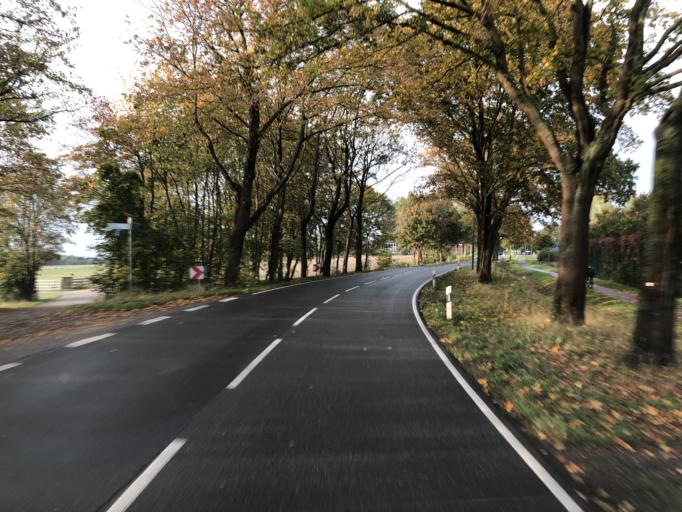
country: DE
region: Lower Saxony
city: Neu Wulmstorf
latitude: 53.4480
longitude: 9.7996
